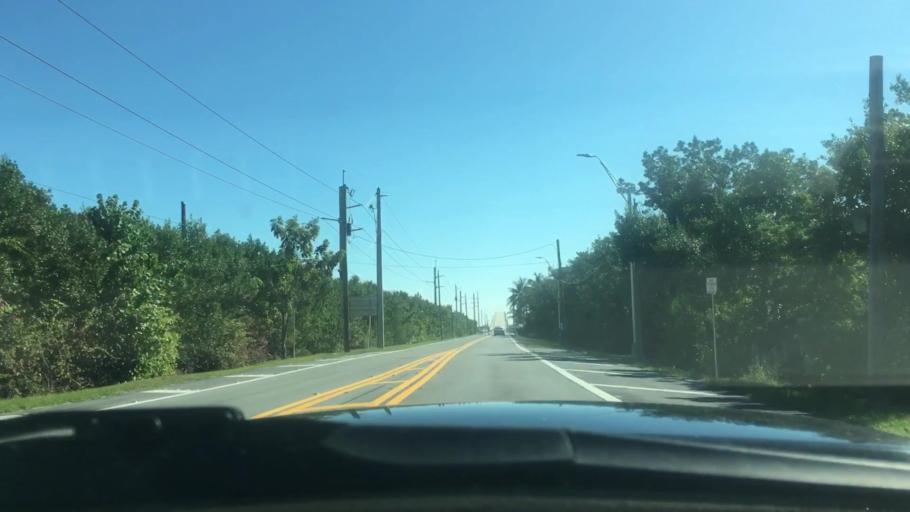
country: US
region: Florida
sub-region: Monroe County
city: North Key Largo
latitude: 25.2909
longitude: -80.3773
